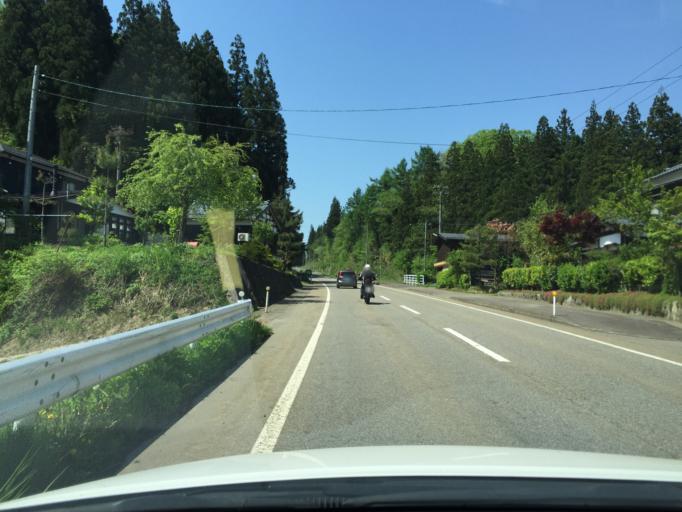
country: JP
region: Niigata
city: Kamo
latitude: 37.6078
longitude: 139.1040
